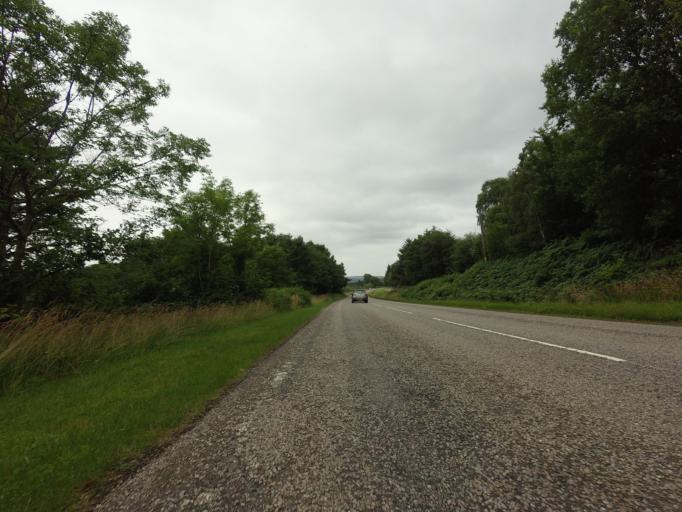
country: GB
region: Scotland
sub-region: Highland
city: Evanton
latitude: 57.9194
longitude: -4.3974
